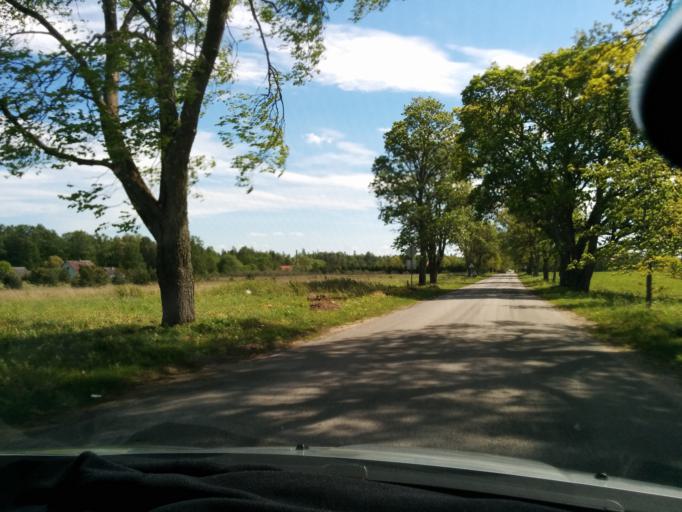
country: EE
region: Harju
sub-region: Loksa linn
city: Loksa
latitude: 59.5160
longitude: 25.9458
